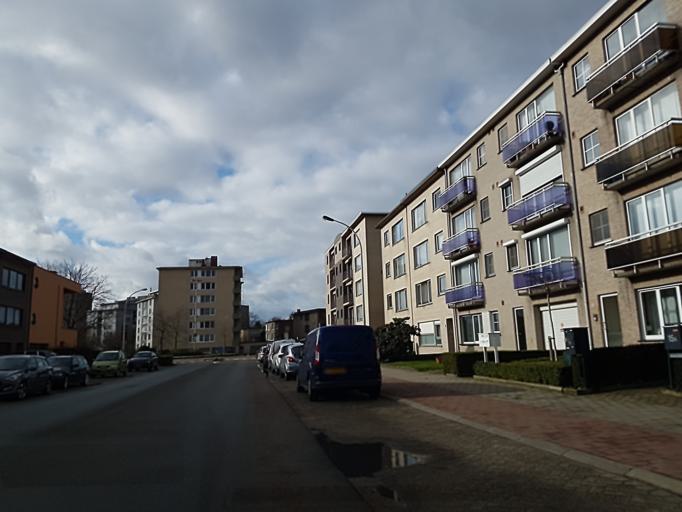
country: BE
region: Flanders
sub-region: Provincie Antwerpen
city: Borsbeek
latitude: 51.2325
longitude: 4.4683
